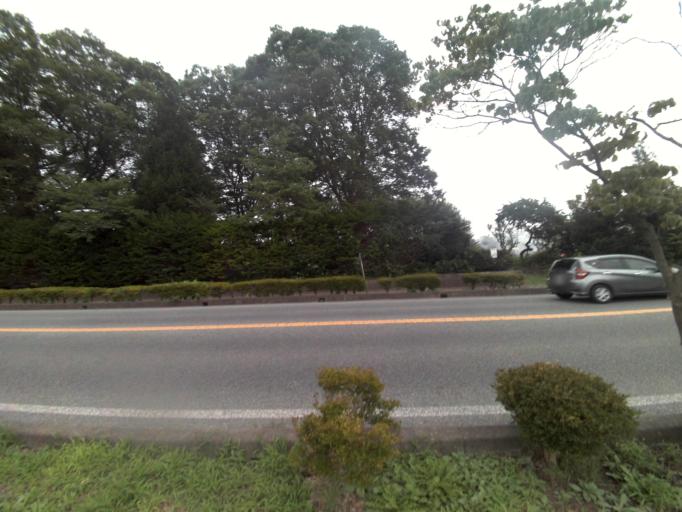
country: JP
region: Nagano
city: Komoro
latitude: 36.2804
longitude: 138.4796
